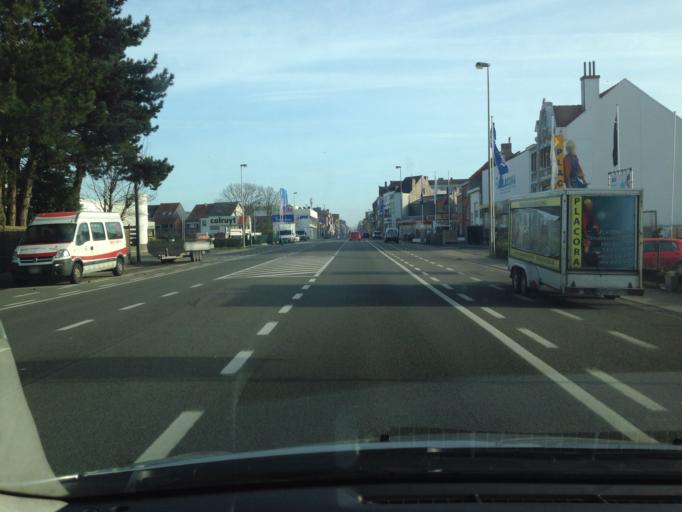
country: BE
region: Flanders
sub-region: Provincie West-Vlaanderen
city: Ostend
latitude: 51.2070
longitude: 2.9046
